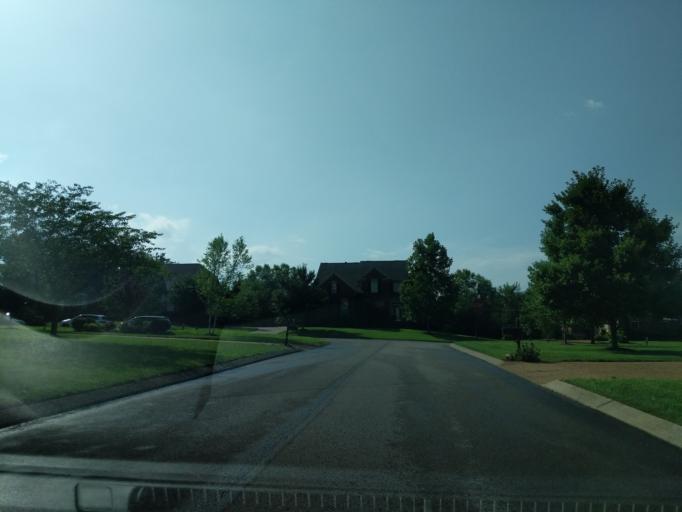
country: US
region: Tennessee
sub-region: Cheatham County
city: Pegram
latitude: 36.0336
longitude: -86.9572
